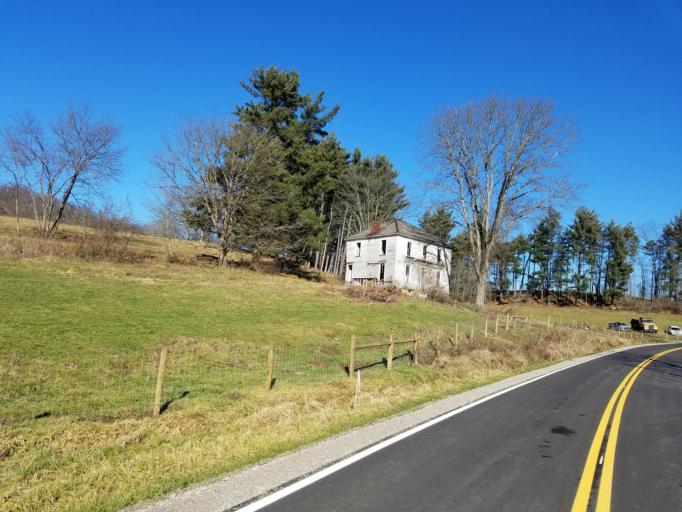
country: US
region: Ohio
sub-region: Belmont County
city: Barnesville
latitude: 40.0385
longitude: -81.2539
